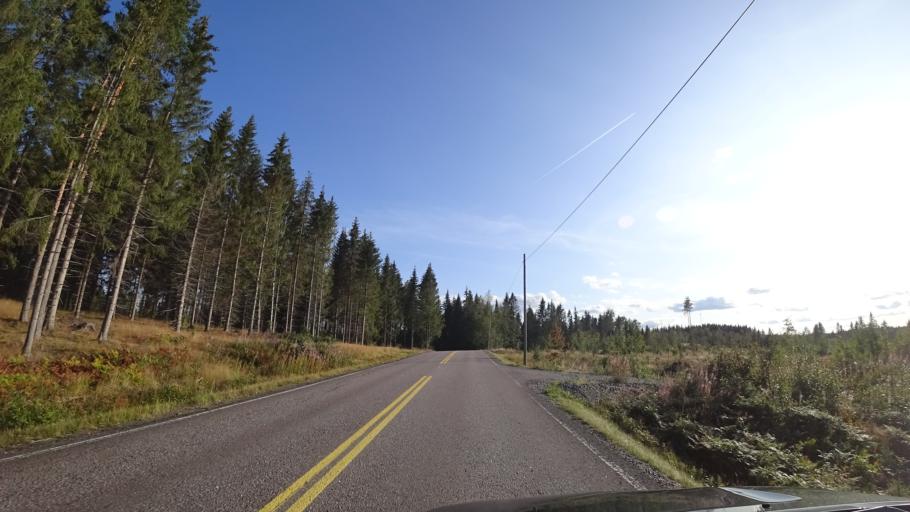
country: FI
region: Paijanne Tavastia
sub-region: Lahti
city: Hollola
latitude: 61.1661
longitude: 25.3633
